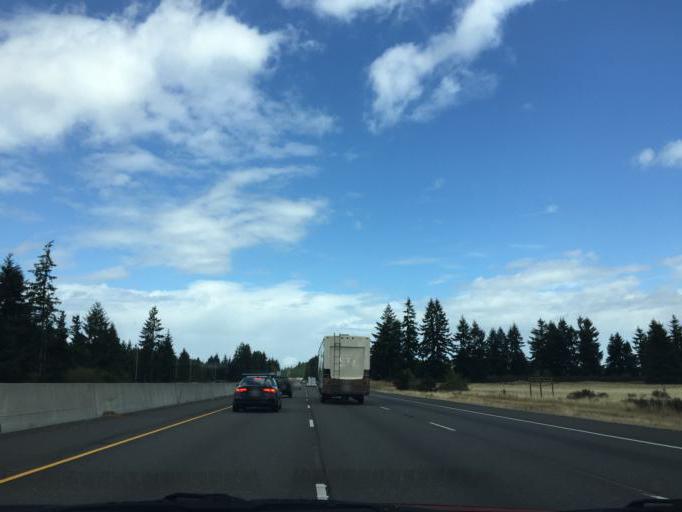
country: US
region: Washington
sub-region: Thurston County
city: Grand Mound
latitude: 46.8479
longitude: -122.9799
